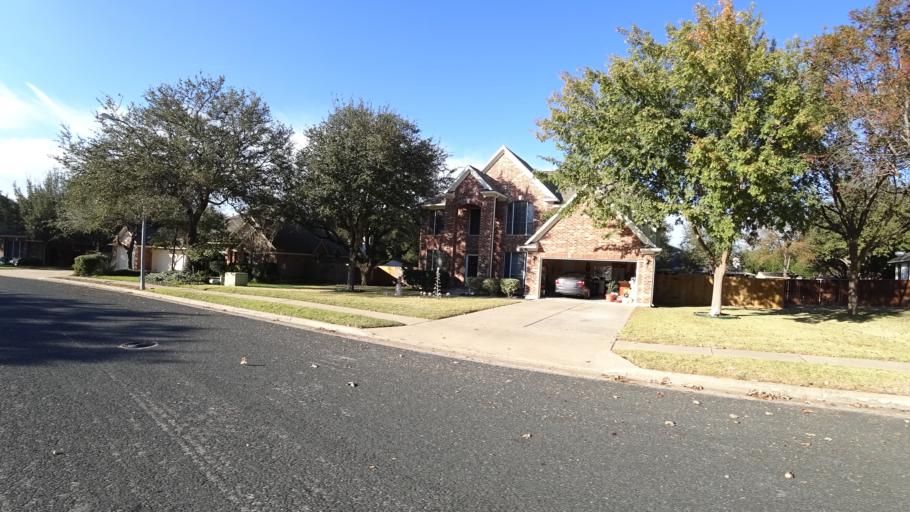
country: US
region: Texas
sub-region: Williamson County
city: Brushy Creek
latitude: 30.4982
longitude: -97.7462
